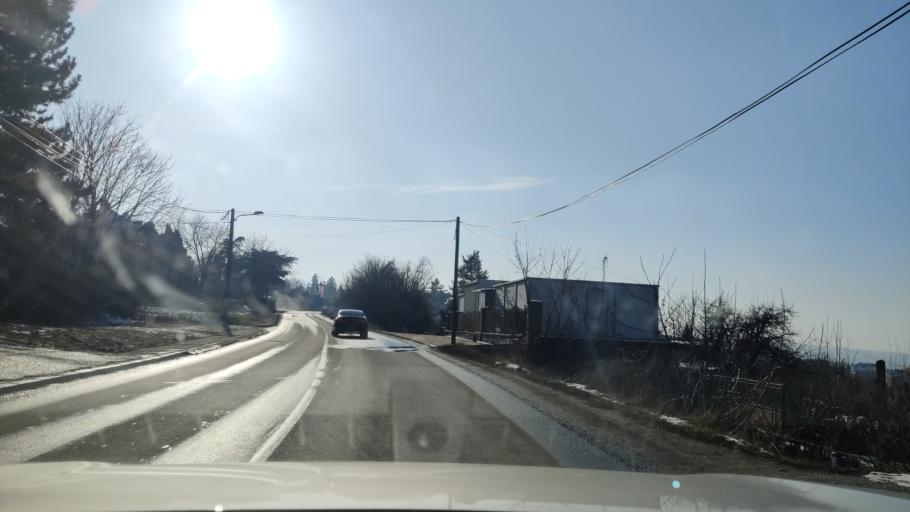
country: RS
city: Rusanj
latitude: 44.7002
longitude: 20.5036
